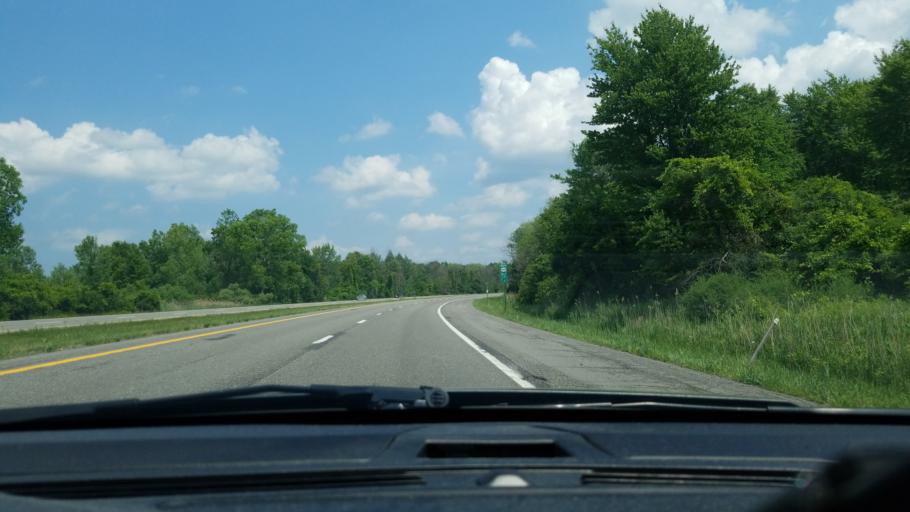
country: US
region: New York
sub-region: Onondaga County
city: Liverpool
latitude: 43.1722
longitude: -76.1907
